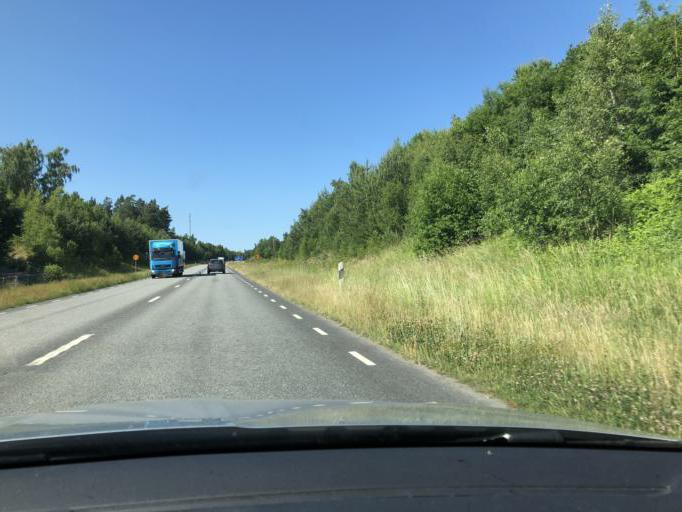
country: SE
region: Skane
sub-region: Bromolla Kommun
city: Bromoella
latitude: 56.0662
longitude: 14.4992
